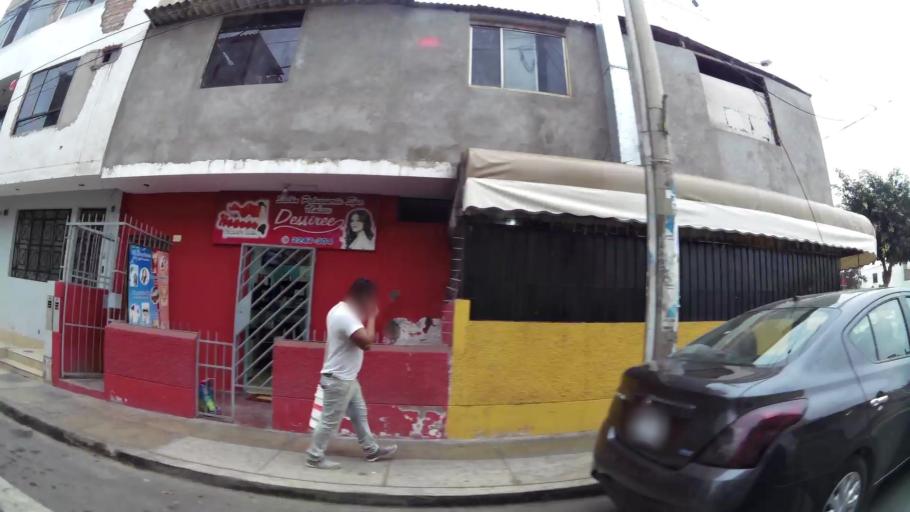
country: PE
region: Lima
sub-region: Lima
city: Surco
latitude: -12.1079
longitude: -77.0106
